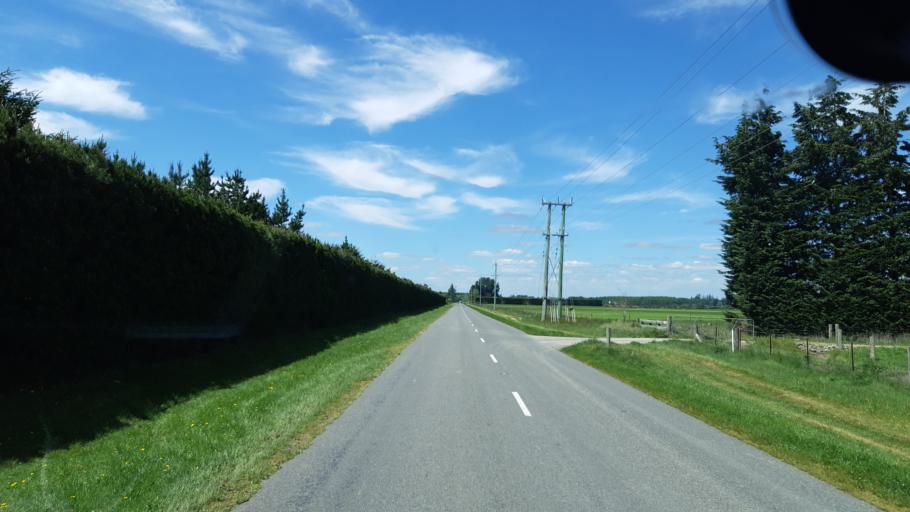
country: NZ
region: Canterbury
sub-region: Ashburton District
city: Methven
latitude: -43.7283
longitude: 171.5052
